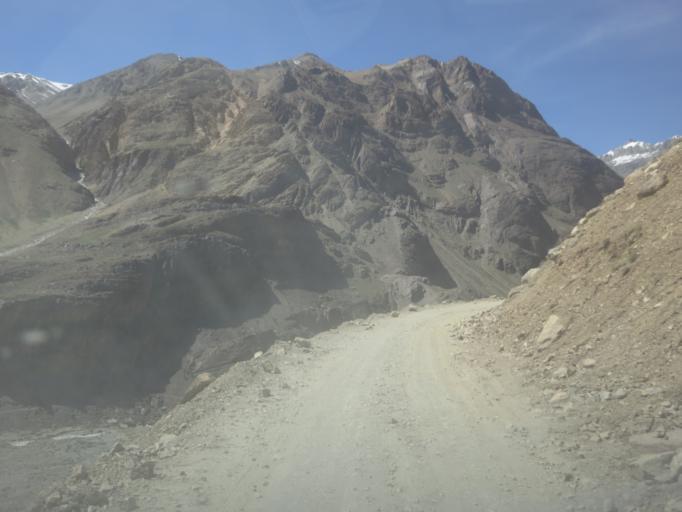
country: IN
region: Himachal Pradesh
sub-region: Kulu
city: Manali
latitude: 32.4308
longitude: 77.6751
